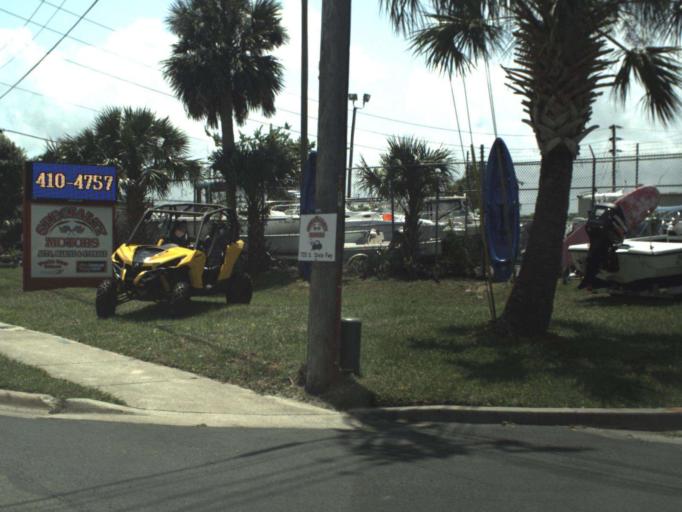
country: US
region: Florida
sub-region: Volusia County
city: New Smyrna Beach
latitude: 29.0155
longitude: -80.9223
